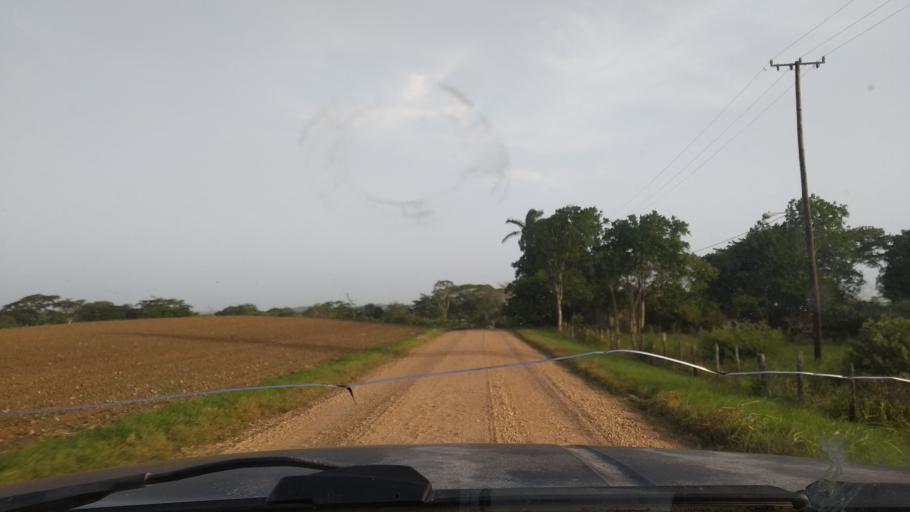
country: BZ
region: Cayo
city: San Ignacio
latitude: 17.2088
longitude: -89.0138
